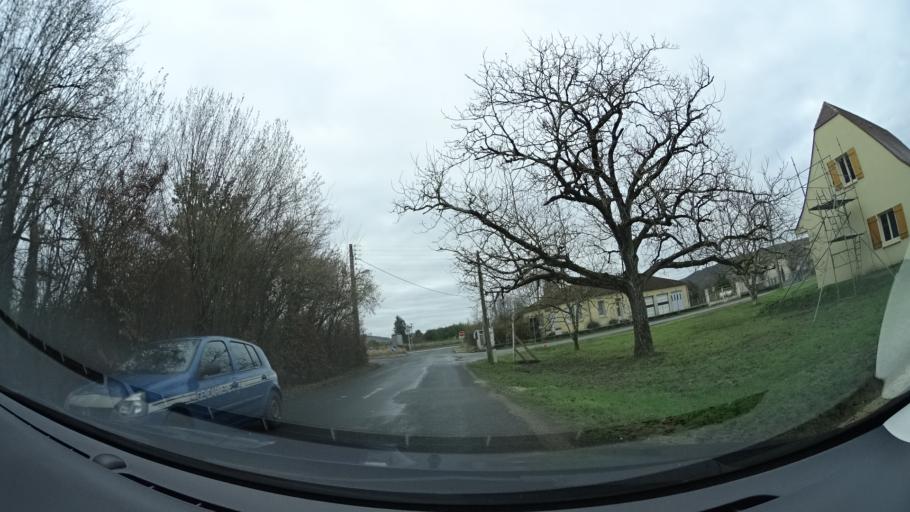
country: FR
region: Aquitaine
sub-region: Departement de la Dordogne
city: Saint-Cyprien
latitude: 44.8651
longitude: 1.0472
